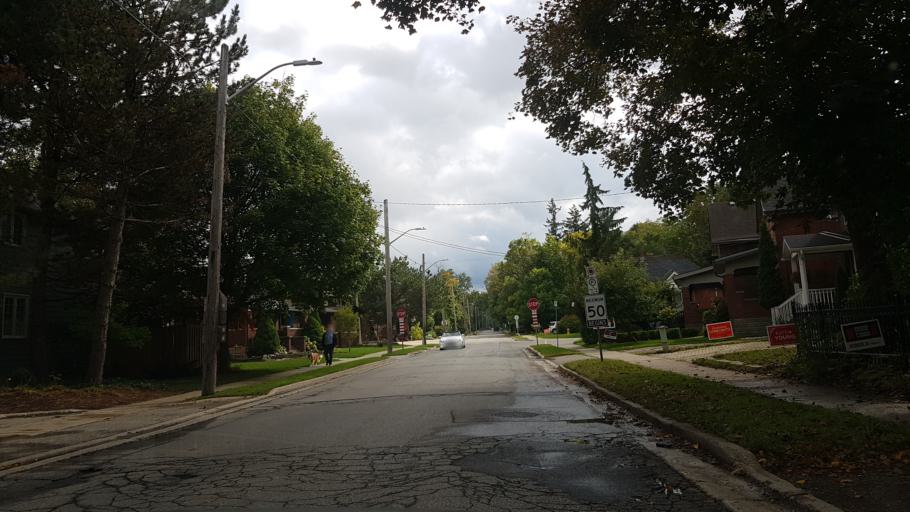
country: CA
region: Ontario
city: London
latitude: 42.9653
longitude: -81.2490
